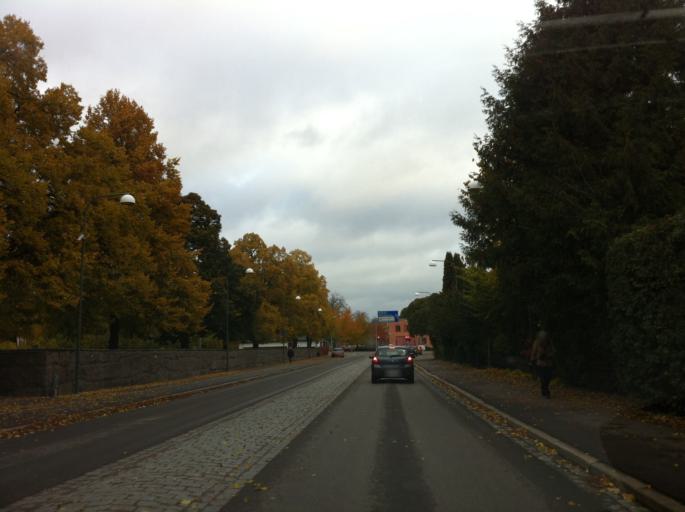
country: SE
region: OEstergoetland
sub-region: Linkopings Kommun
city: Linkoping
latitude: 58.4080
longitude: 15.6092
